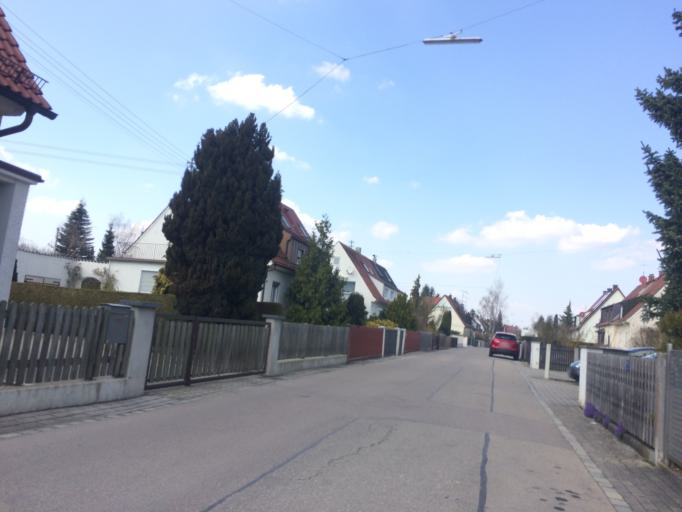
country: DE
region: Bavaria
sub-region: Swabia
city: Augsburg
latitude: 48.3986
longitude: 10.8974
